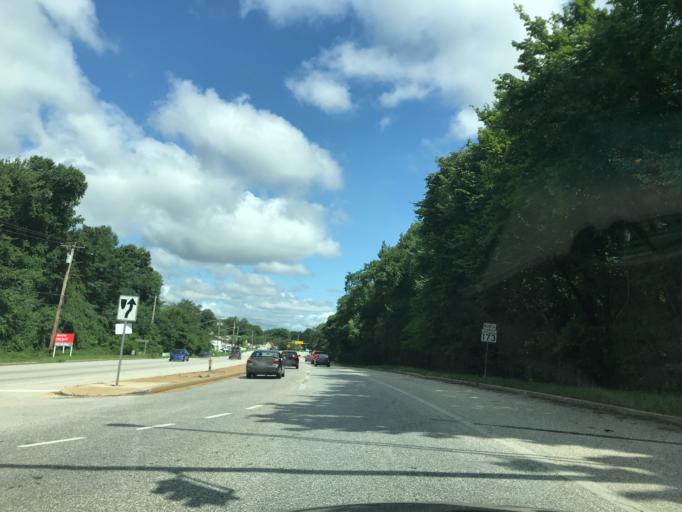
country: US
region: Maryland
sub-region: Anne Arundel County
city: Green Haven
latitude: 39.1876
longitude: -76.5522
